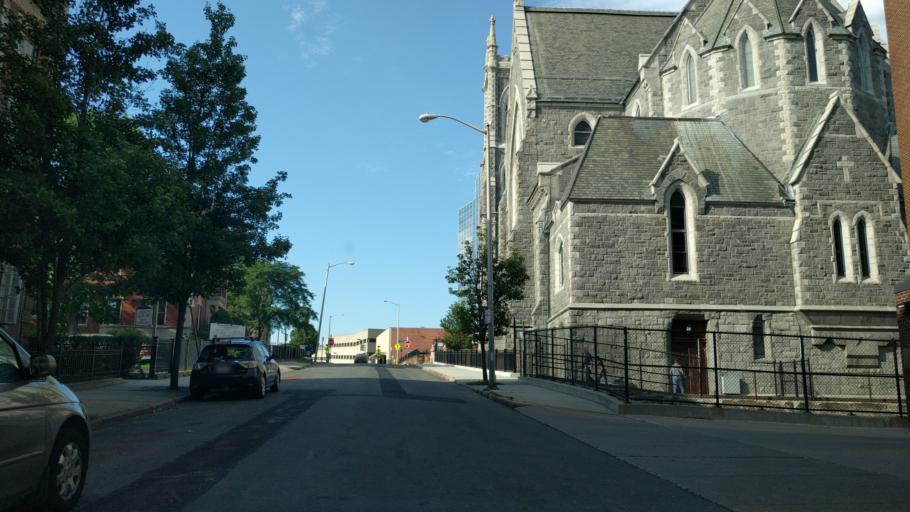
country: US
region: Massachusetts
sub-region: Worcester County
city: Worcester
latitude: 42.2612
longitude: -71.8047
